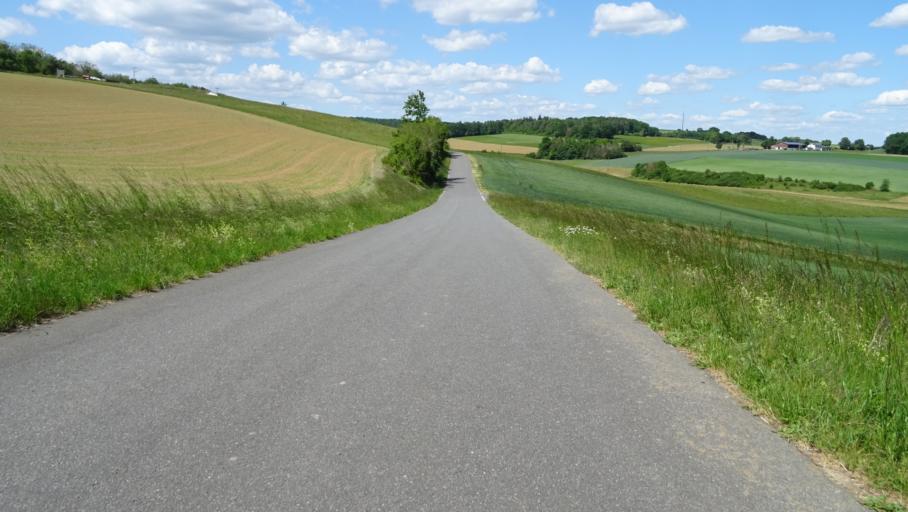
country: DE
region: Baden-Wuerttemberg
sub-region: Karlsruhe Region
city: Seckach
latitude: 49.4132
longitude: 9.3497
